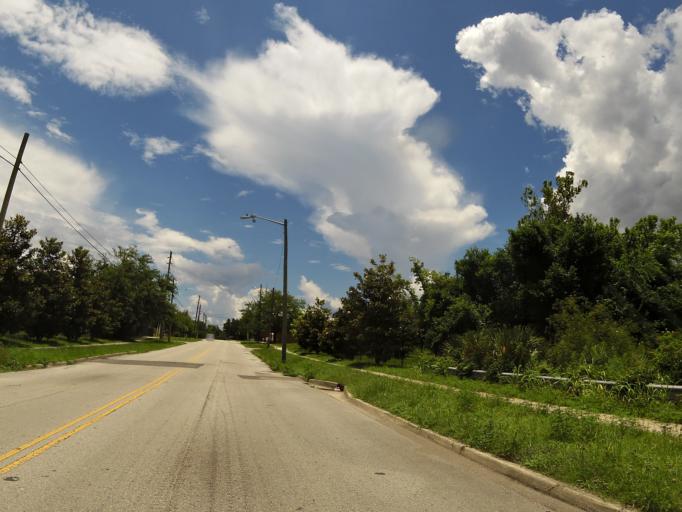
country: US
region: Florida
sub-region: Duval County
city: Jacksonville
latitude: 30.3448
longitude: -81.6670
